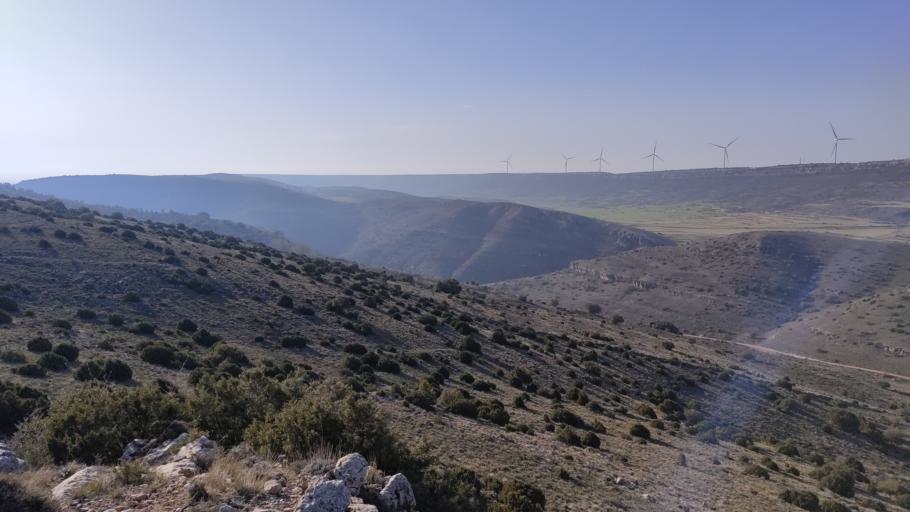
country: ES
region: Aragon
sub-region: Provincia de Teruel
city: Allueva
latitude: 41.0151
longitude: -1.0367
